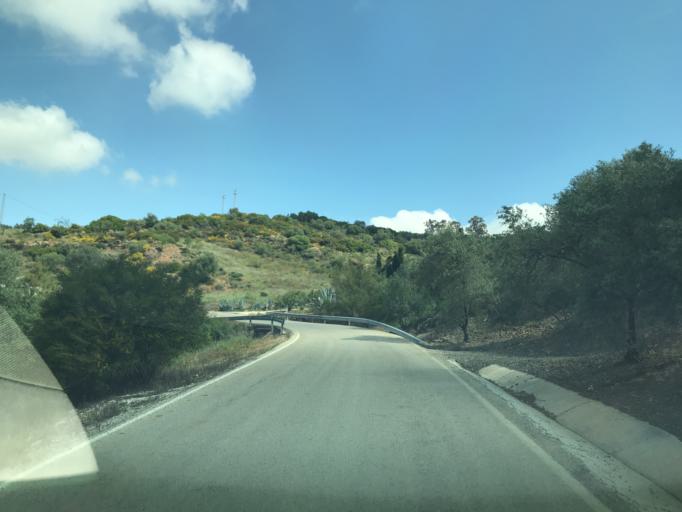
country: ES
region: Andalusia
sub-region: Provincia de Malaga
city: Periana
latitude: 36.9236
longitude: -4.1772
